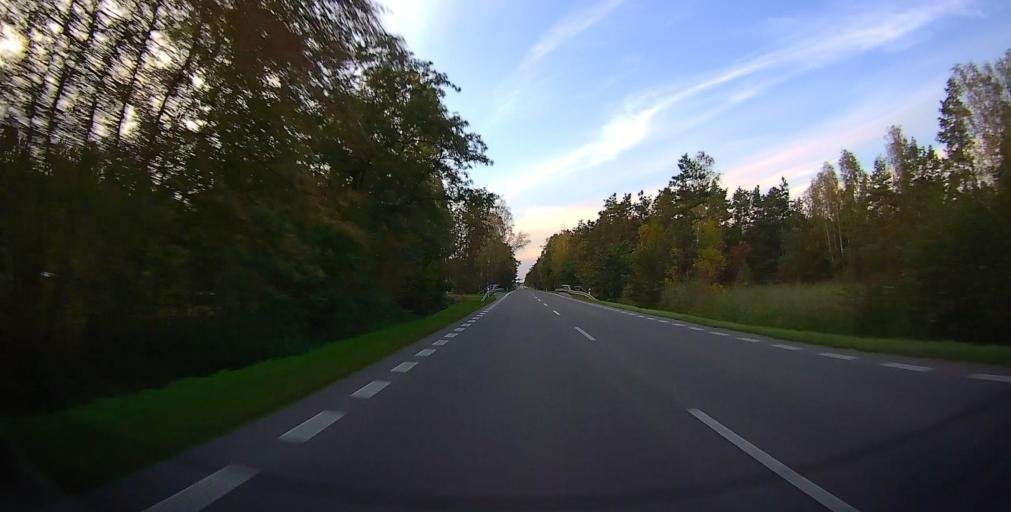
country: PL
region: Masovian Voivodeship
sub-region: Powiat kozienicki
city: Ryczywol
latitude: 51.6735
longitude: 21.4381
